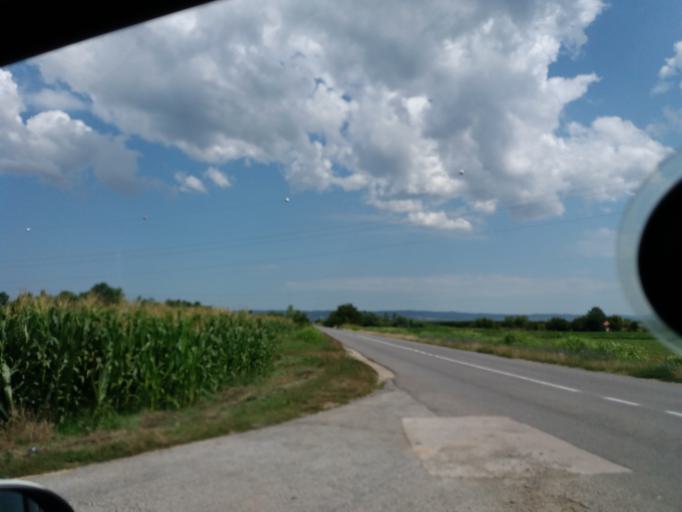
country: RS
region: Autonomna Pokrajina Vojvodina
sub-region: Sremski Okrug
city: Sremska Mitrovica
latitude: 45.0027
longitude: 19.6428
